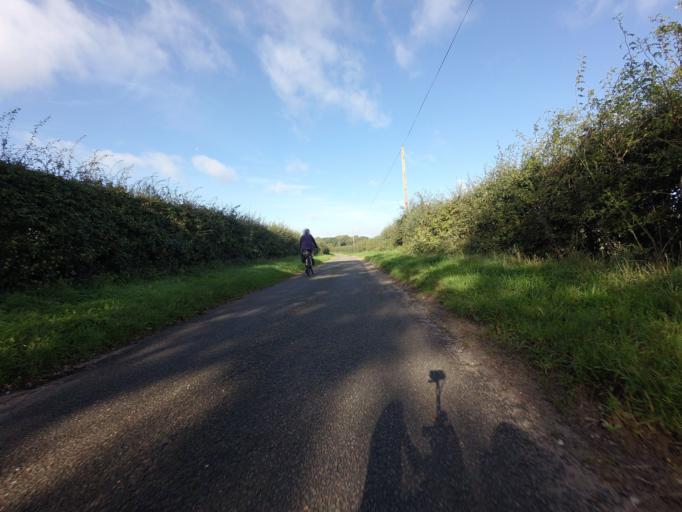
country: GB
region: England
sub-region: Norfolk
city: Fakenham
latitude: 52.8474
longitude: 0.6766
